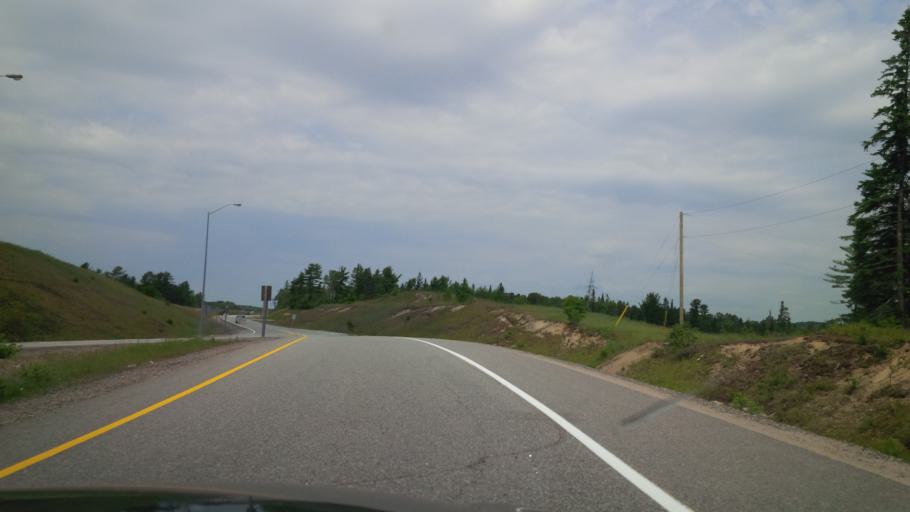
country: CA
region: Ontario
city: Huntsville
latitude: 45.5126
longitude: -79.3049
